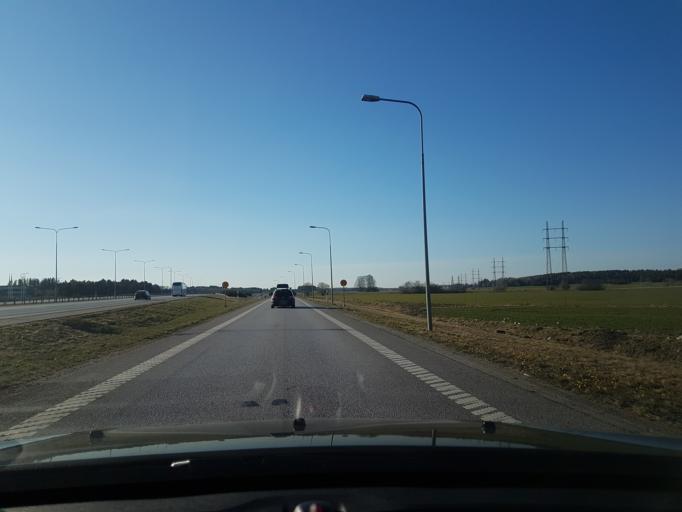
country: SE
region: Uppsala
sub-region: Uppsala Kommun
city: Gamla Uppsala
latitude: 59.8860
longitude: 17.6760
